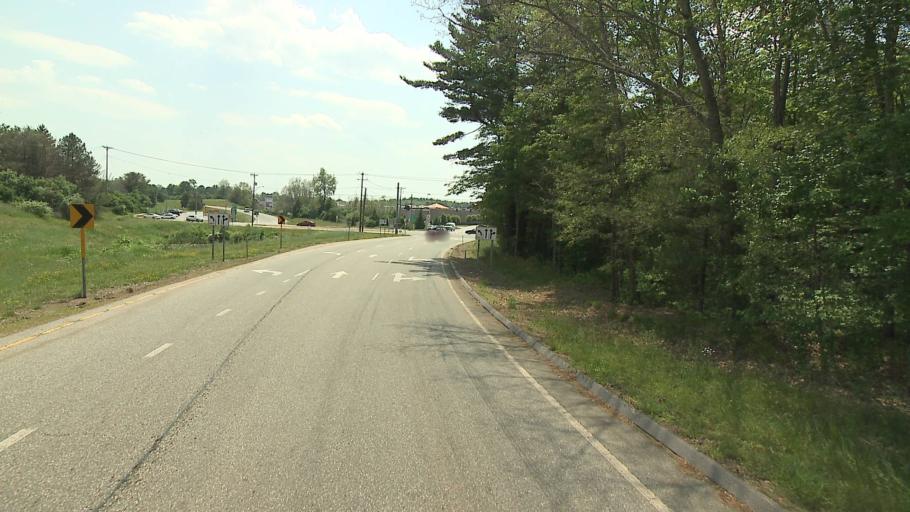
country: US
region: Connecticut
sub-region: Windham County
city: Killingly Center
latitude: 41.8441
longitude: -71.8798
